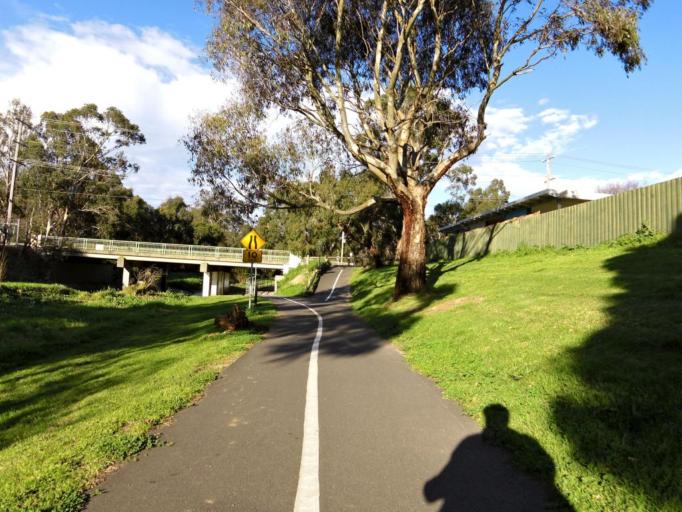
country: AU
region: Victoria
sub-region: Knox
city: Wantirna
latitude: -37.8395
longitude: 145.2267
